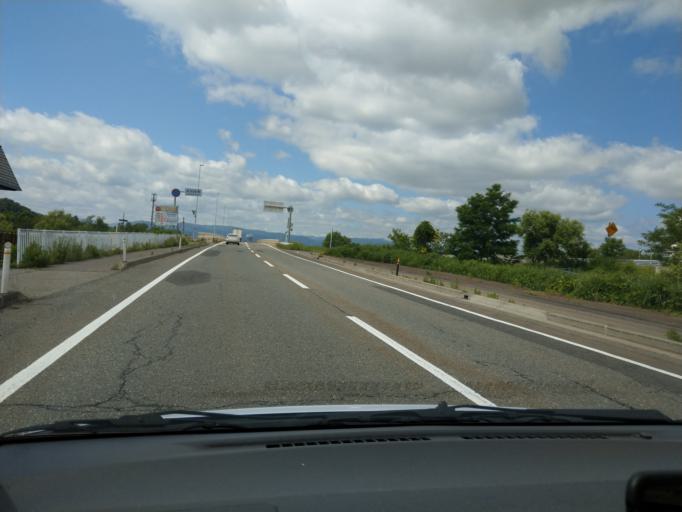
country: JP
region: Akita
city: Yuzawa
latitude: 39.2116
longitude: 140.5124
